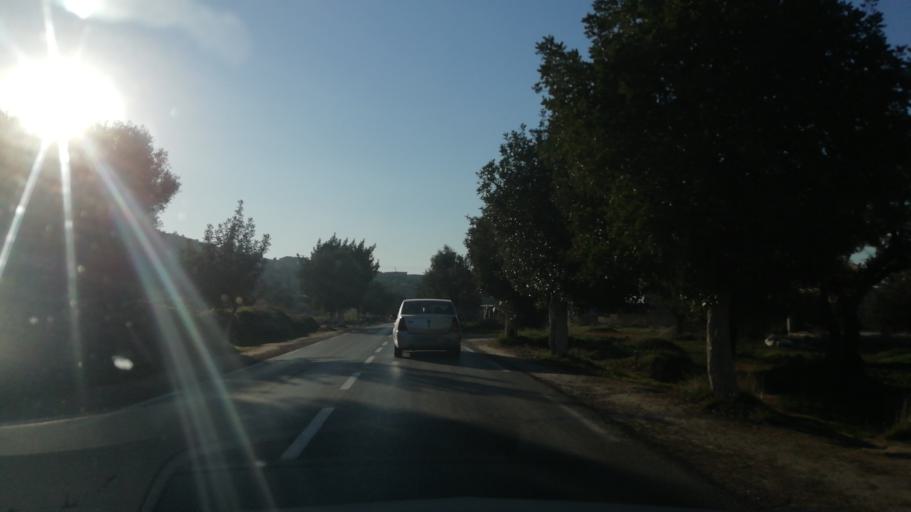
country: DZ
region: Tlemcen
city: Beni Mester
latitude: 34.8606
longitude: -1.4401
